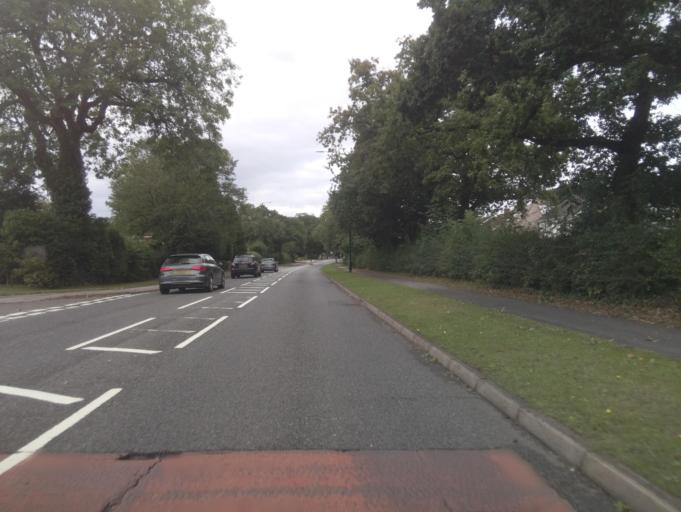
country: GB
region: England
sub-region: Solihull
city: Cheswick Green
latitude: 52.3559
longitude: -1.7787
